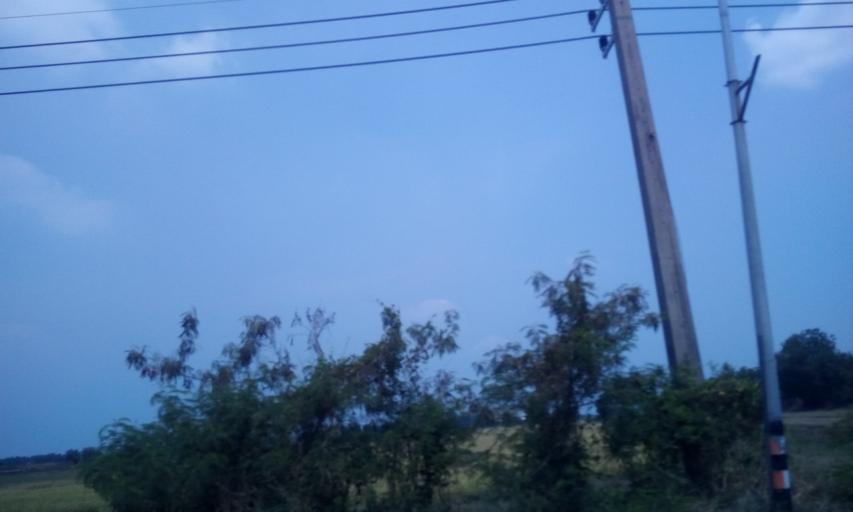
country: TH
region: Bangkok
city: Nong Chok
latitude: 13.9617
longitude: 100.9031
